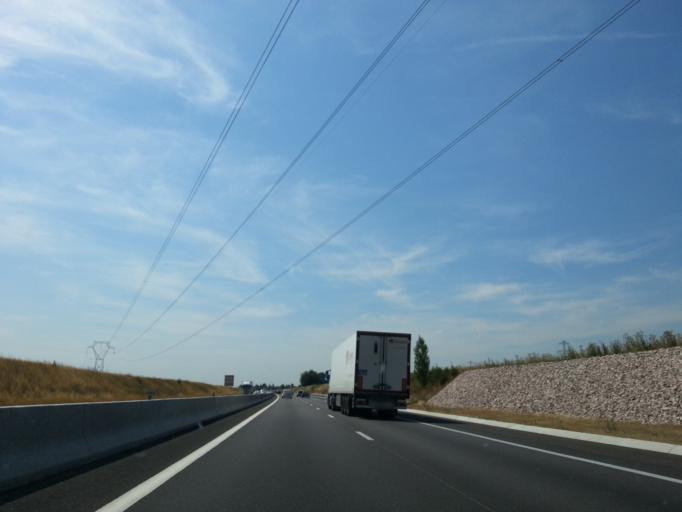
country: FR
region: Alsace
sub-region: Departement du Bas-Rhin
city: Kintzheim
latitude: 48.2543
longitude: 7.4130
